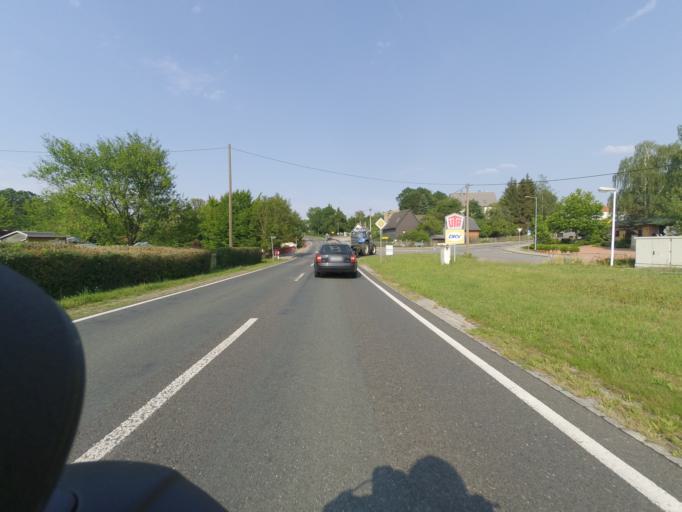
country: DE
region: Saxony
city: Geringswalde
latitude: 51.0727
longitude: 12.8959
